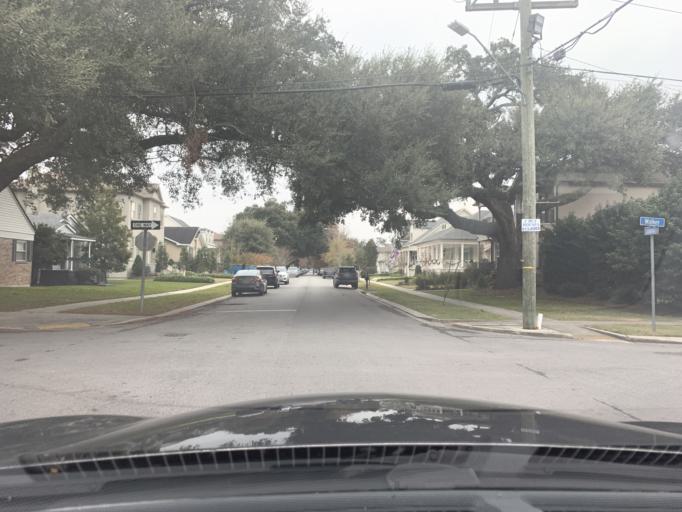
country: US
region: Louisiana
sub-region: Jefferson Parish
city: Metairie
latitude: 30.0180
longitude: -90.1088
